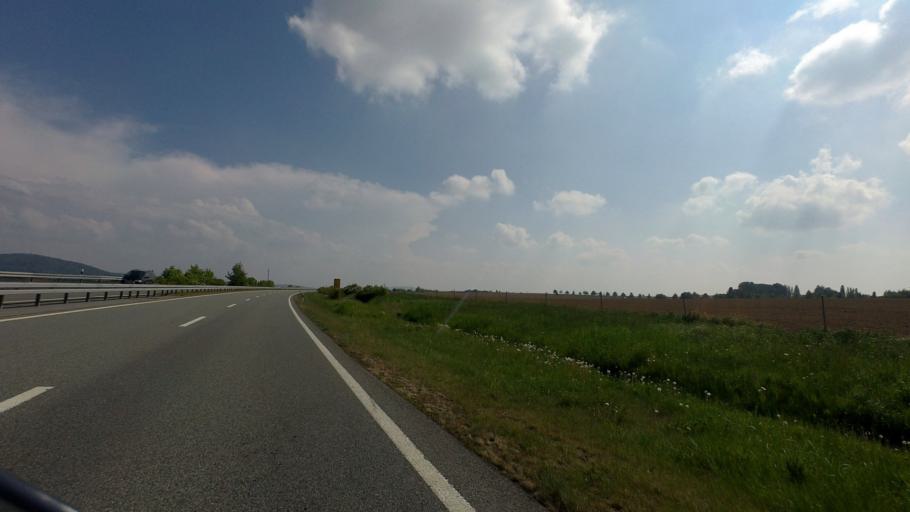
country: DE
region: Saxony
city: Lobau
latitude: 51.1196
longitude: 14.6496
